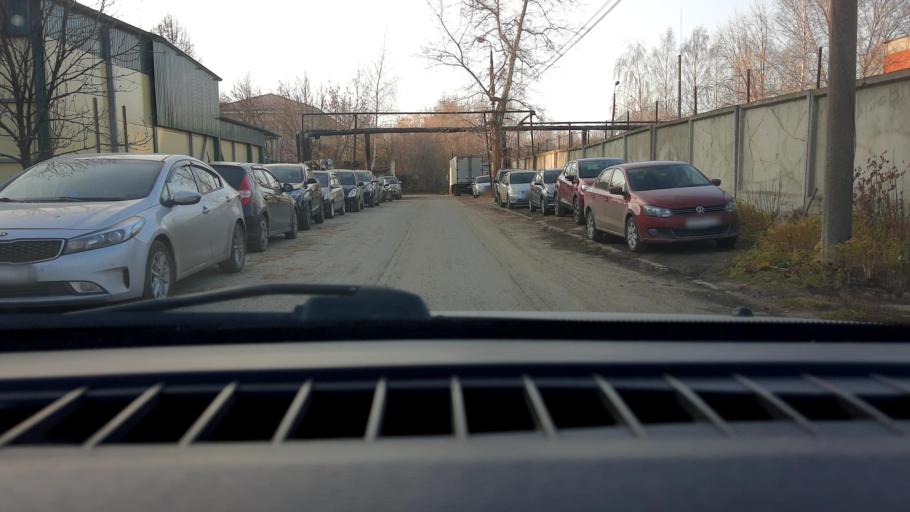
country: RU
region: Nizjnij Novgorod
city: Gorbatovka
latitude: 56.3193
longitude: 43.8594
